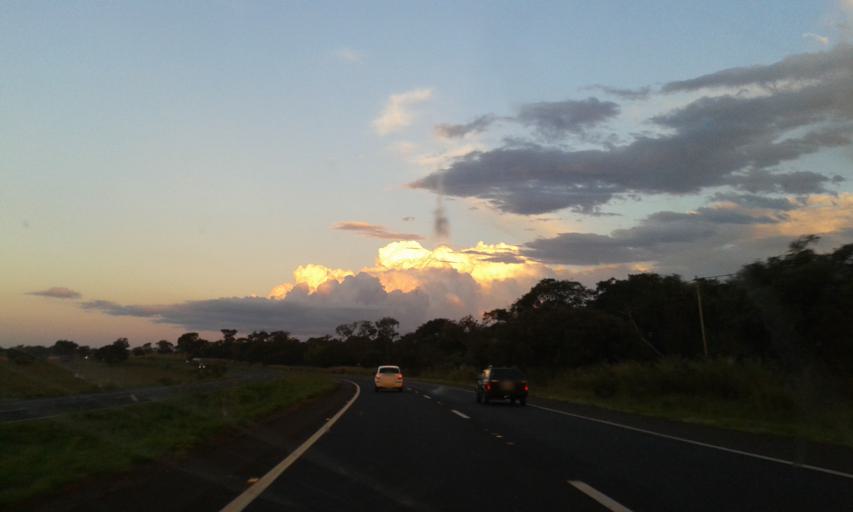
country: BR
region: Minas Gerais
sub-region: Monte Alegre De Minas
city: Monte Alegre de Minas
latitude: -18.8942
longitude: -48.6591
